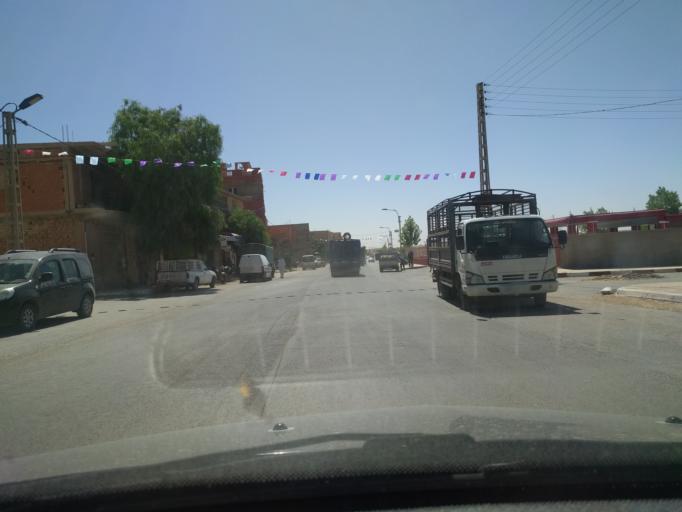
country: DZ
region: Tiaret
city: Frenda
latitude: 34.9051
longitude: 1.1092
